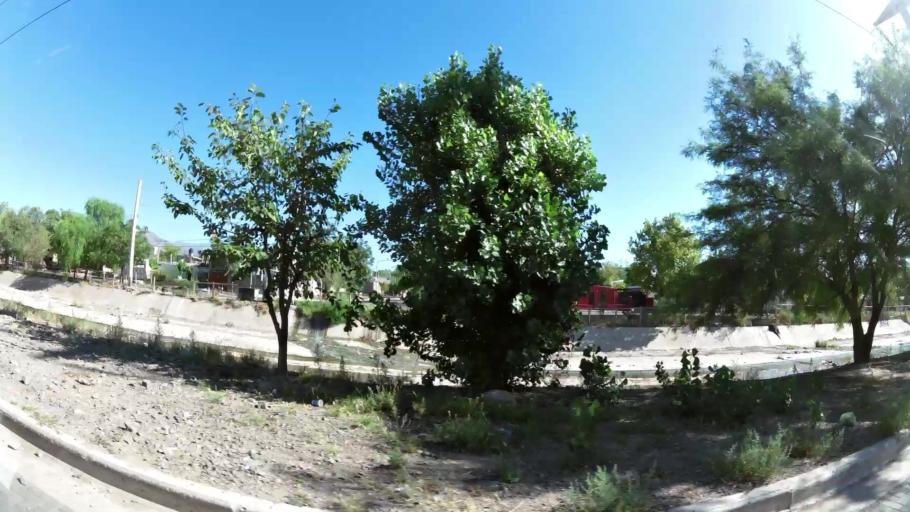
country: AR
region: Mendoza
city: Las Heras
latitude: -32.8716
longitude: -68.8659
